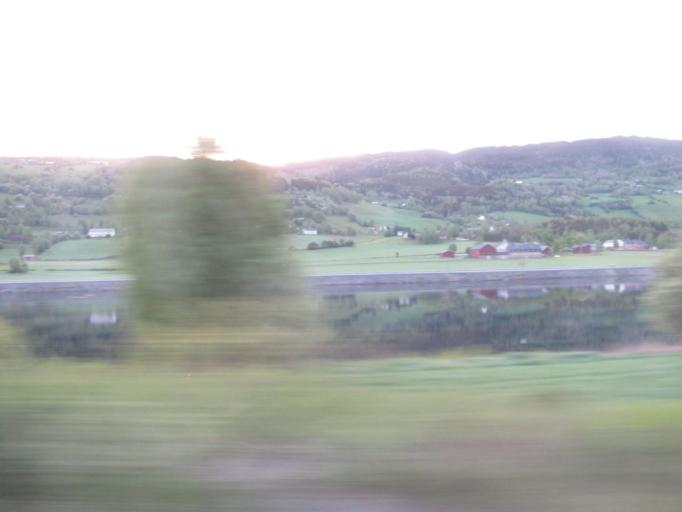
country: NO
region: Oppland
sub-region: Oyer
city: Tretten
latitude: 61.2573
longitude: 10.4173
